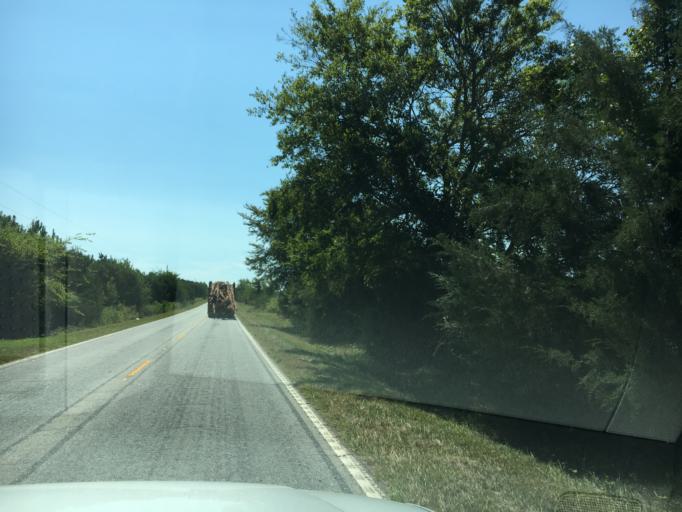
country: US
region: South Carolina
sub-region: Laurens County
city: Joanna
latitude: 34.4012
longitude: -81.8547
